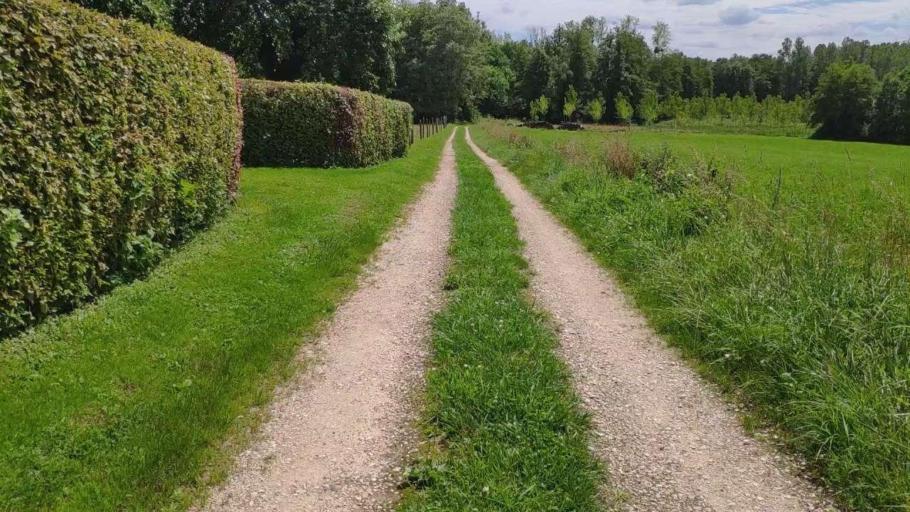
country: FR
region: Franche-Comte
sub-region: Departement du Jura
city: Chaussin
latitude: 46.9004
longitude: 5.4512
